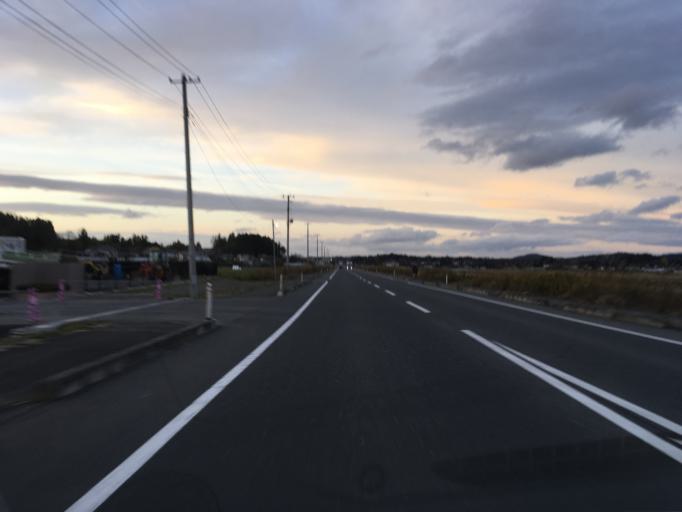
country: JP
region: Iwate
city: Ichinoseki
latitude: 38.7342
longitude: 141.2590
